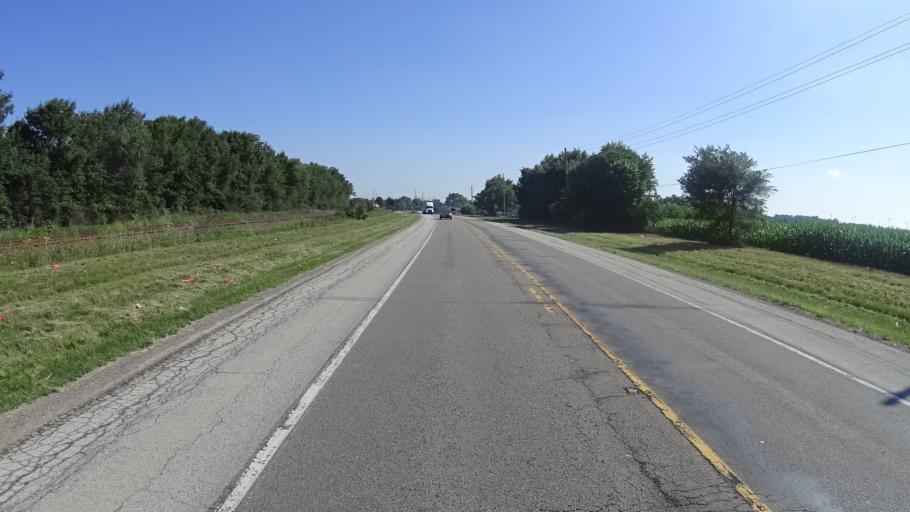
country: US
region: Indiana
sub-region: Madison County
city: Pendleton
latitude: 39.9924
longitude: -85.7397
